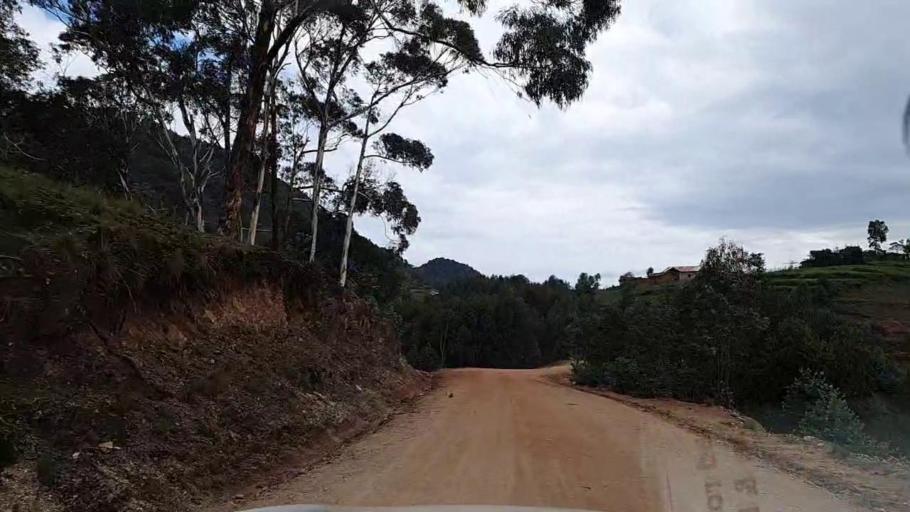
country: RW
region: Southern Province
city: Nzega
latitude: -2.3935
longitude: 29.4521
